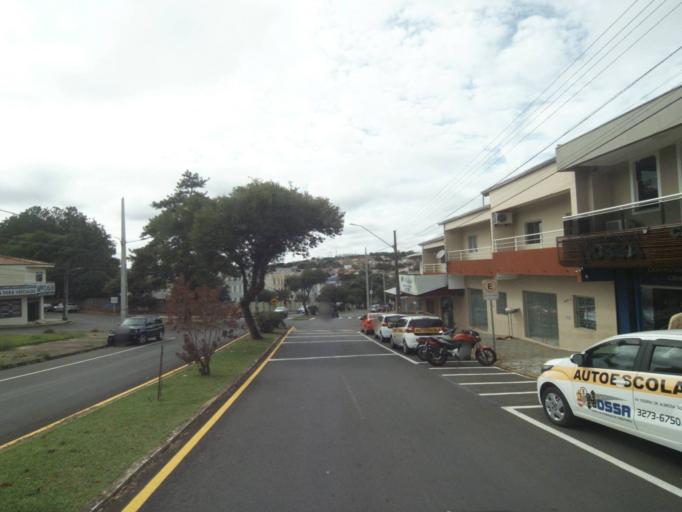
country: BR
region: Parana
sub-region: Telemaco Borba
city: Telemaco Borba
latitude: -24.3329
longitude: -50.6163
